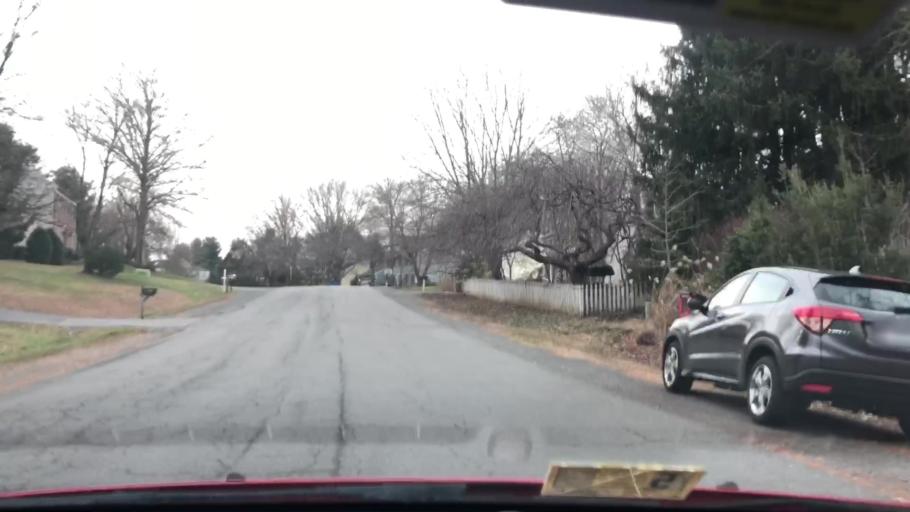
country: US
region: Virginia
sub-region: Fairfax County
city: Wolf Trap
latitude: 38.9651
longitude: -77.2818
